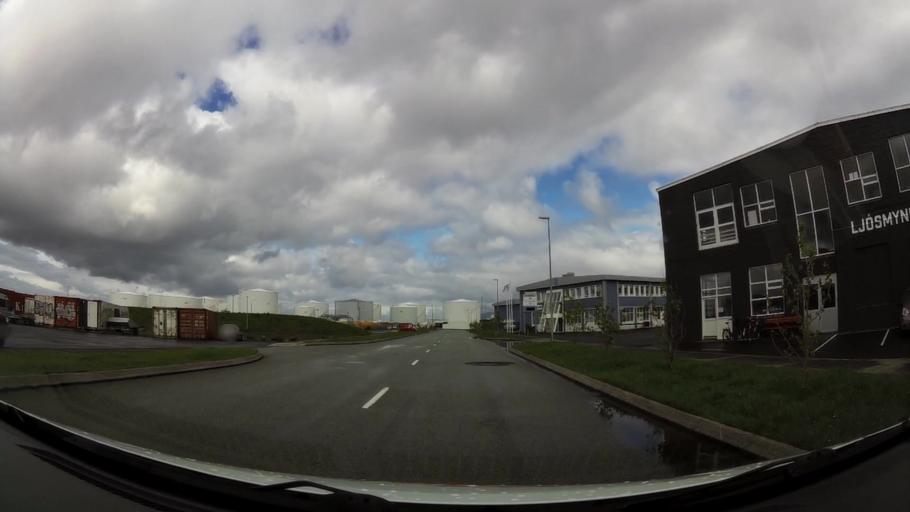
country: IS
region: Capital Region
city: Reykjavik
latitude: 64.1575
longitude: -21.9414
